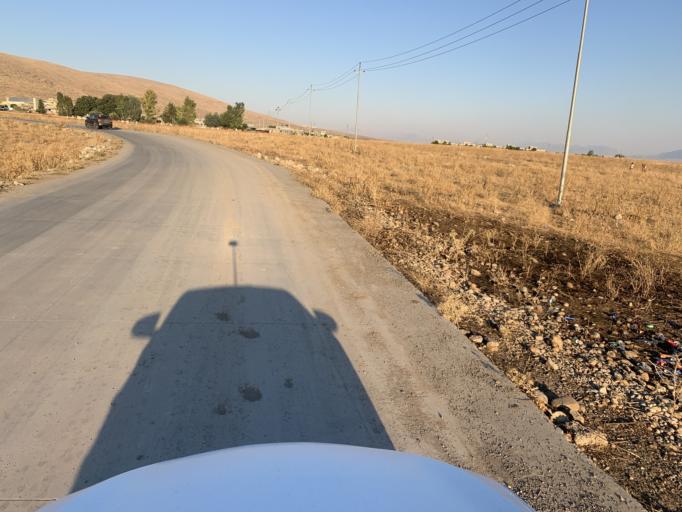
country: IQ
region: As Sulaymaniyah
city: Raniye
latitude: 36.2713
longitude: 44.7555
